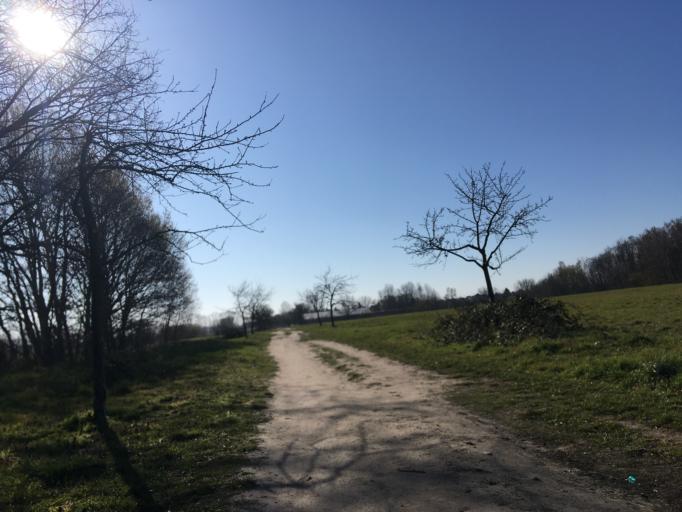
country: DE
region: Berlin
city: Buchholz
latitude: 52.6242
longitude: 13.4160
